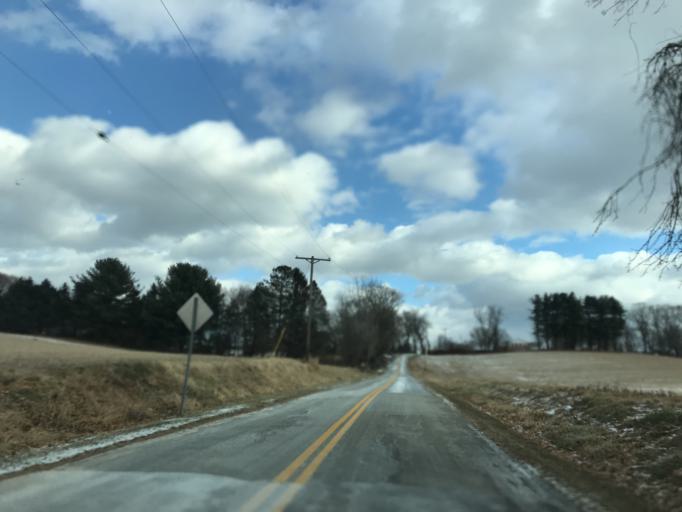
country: US
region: Maryland
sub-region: Harford County
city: Jarrettsville
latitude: 39.6386
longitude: -76.5104
